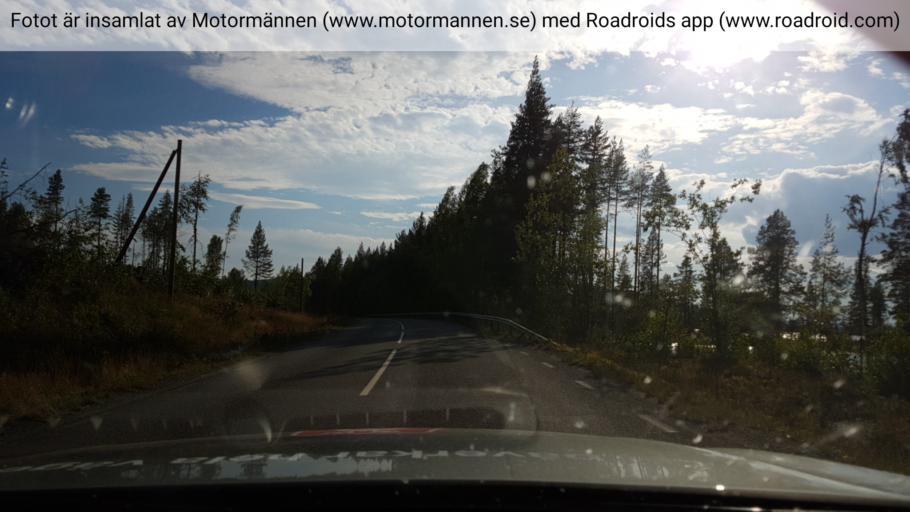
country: SE
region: Vaesternorrland
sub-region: Solleftea Kommun
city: As
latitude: 63.5811
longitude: 16.3136
